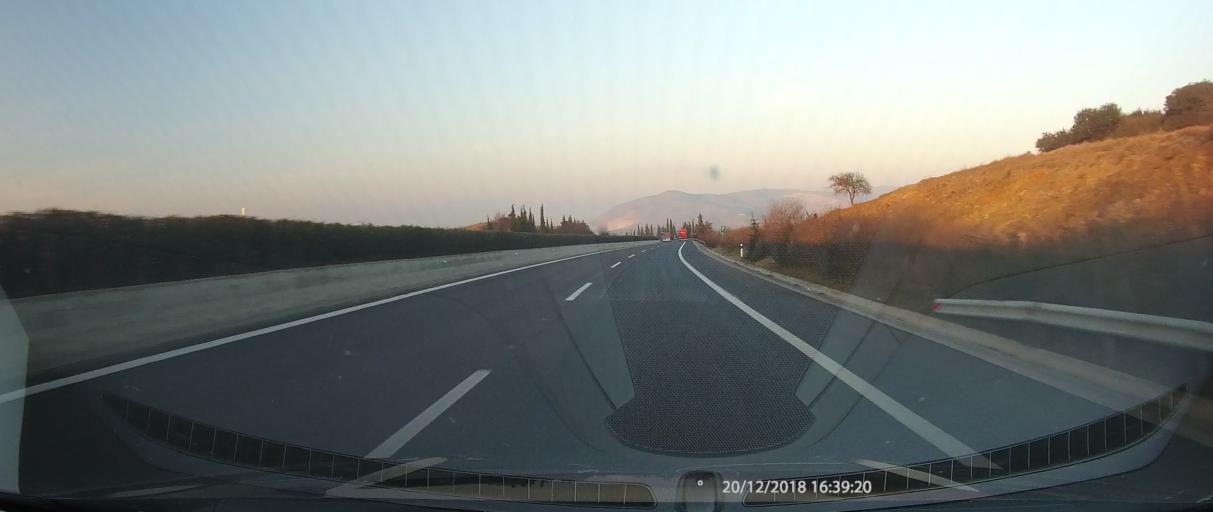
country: GR
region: Thessaly
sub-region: Nomos Magnisias
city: Velestino
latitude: 39.3565
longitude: 22.7729
